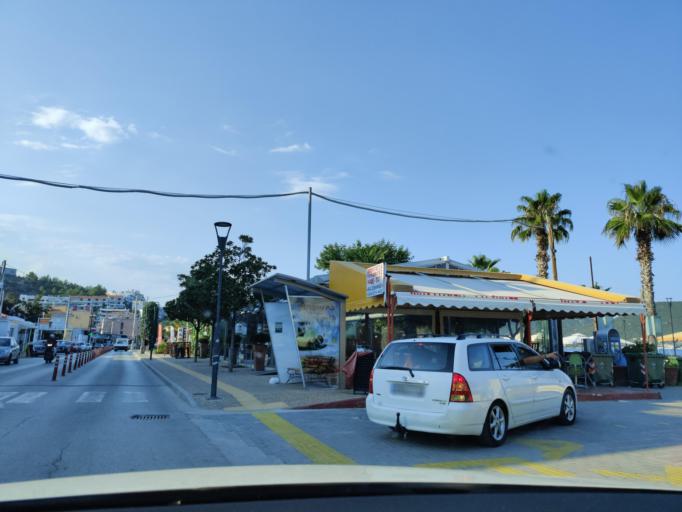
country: GR
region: East Macedonia and Thrace
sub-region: Nomos Kavalas
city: Nea Peramos
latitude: 40.8396
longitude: 24.3050
